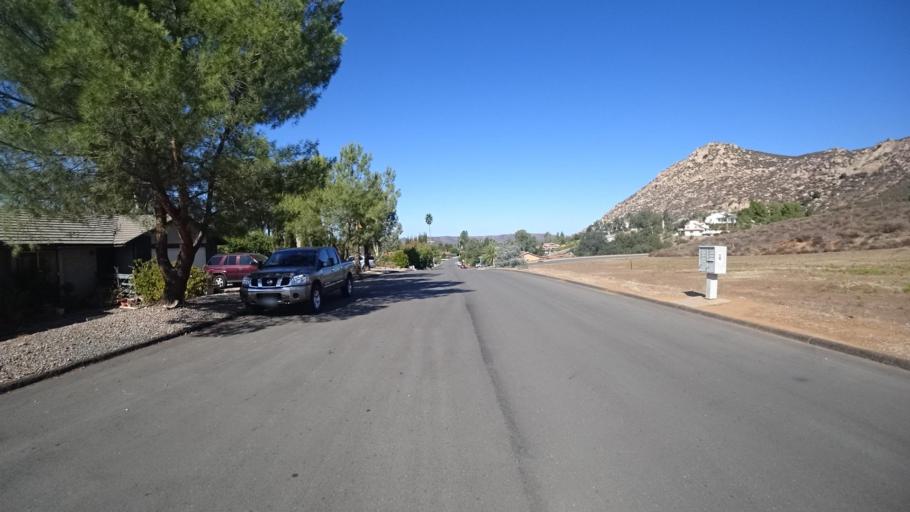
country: US
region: California
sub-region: San Diego County
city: San Diego Country Estates
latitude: 33.0021
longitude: -116.7678
